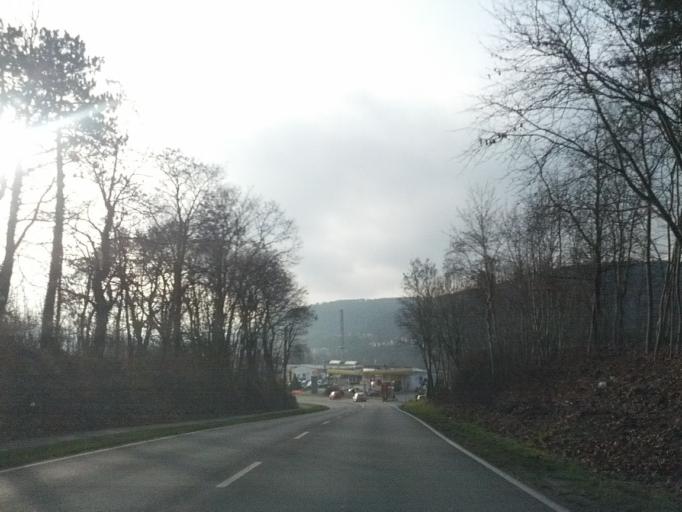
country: DE
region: Thuringia
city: Meiningen
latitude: 50.5910
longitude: 10.4122
